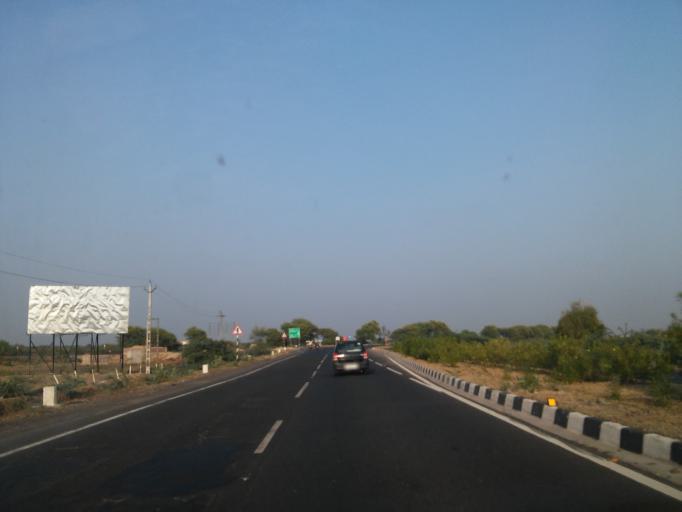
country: IN
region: Gujarat
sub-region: Ahmadabad
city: Sanand
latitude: 23.0789
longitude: 72.1841
